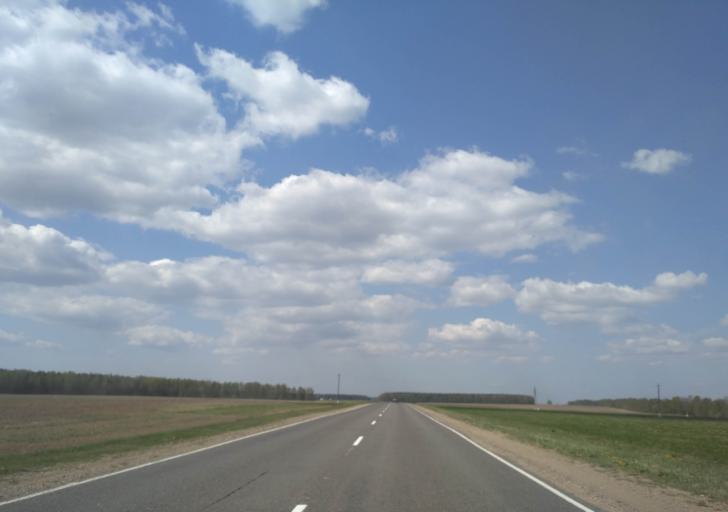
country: BY
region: Minsk
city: Vilyeyka
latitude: 54.5143
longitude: 27.0433
